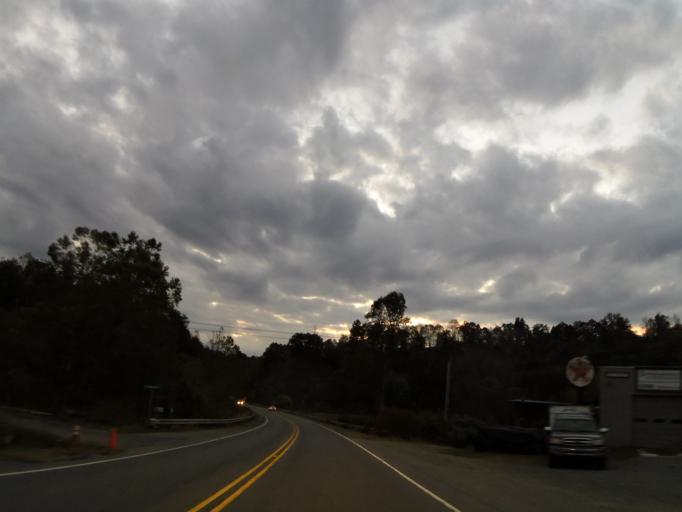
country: US
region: North Carolina
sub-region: Madison County
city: Marshall
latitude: 35.8151
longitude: -82.6843
